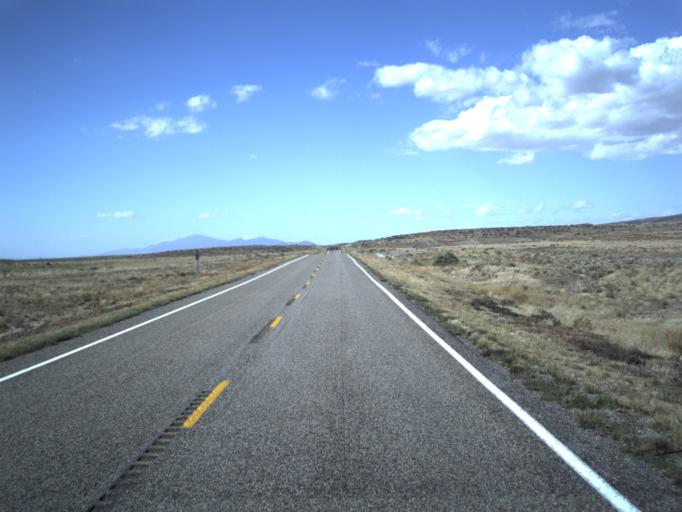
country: US
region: Utah
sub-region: Beaver County
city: Milford
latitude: 38.7953
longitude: -112.9014
